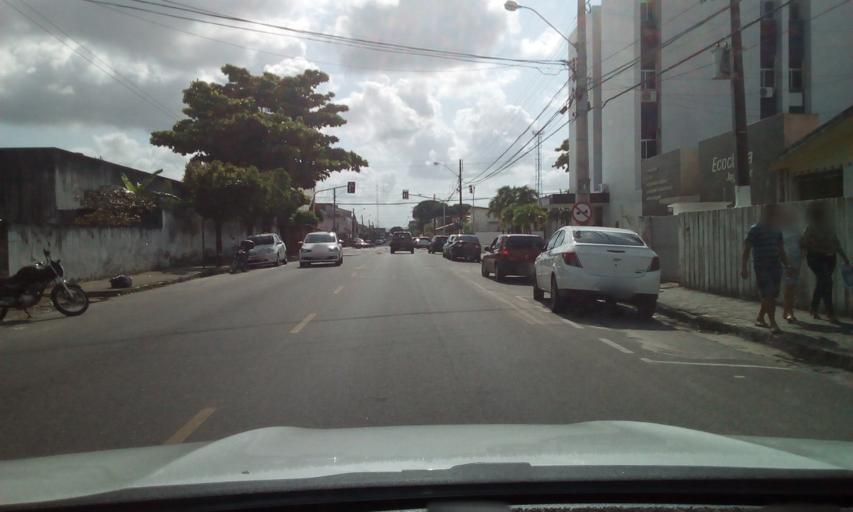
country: BR
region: Paraiba
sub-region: Joao Pessoa
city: Joao Pessoa
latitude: -7.1302
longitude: -34.8738
